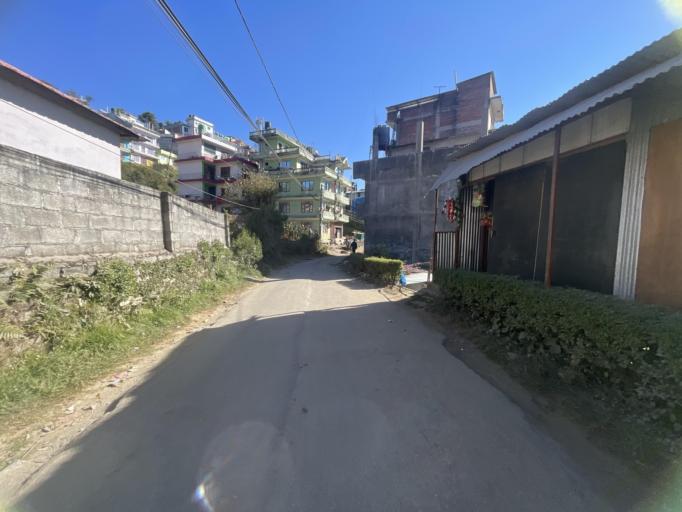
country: NP
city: Kodari
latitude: 27.6672
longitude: 86.0456
